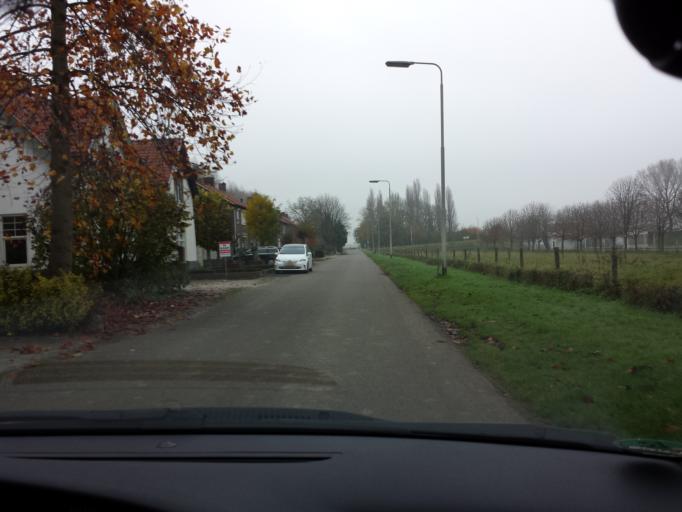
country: NL
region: Limburg
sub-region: Gemeente Maasgouw
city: Maasbracht
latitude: 51.1759
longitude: 5.9229
